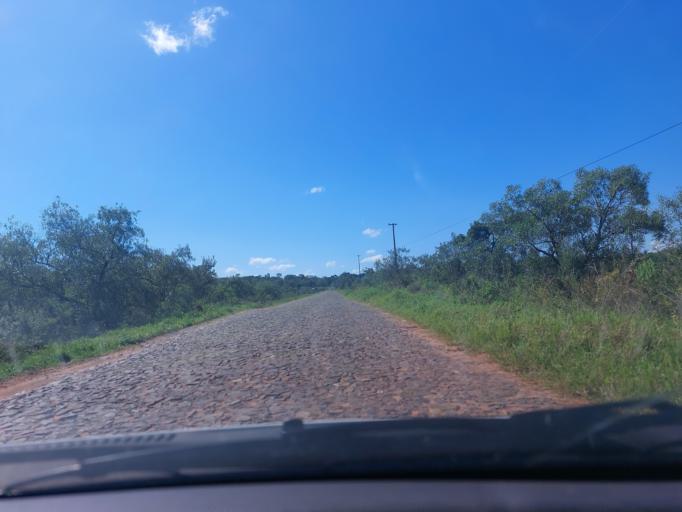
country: PY
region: San Pedro
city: Itacurubi del Rosario
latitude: -24.5874
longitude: -56.6014
